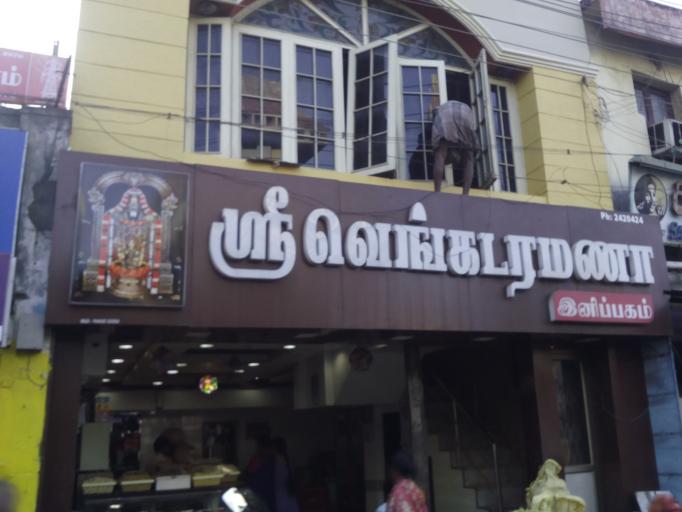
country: IN
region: Tamil Nadu
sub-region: Thanjavur
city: Kumbakonam
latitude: 10.9583
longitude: 79.3808
